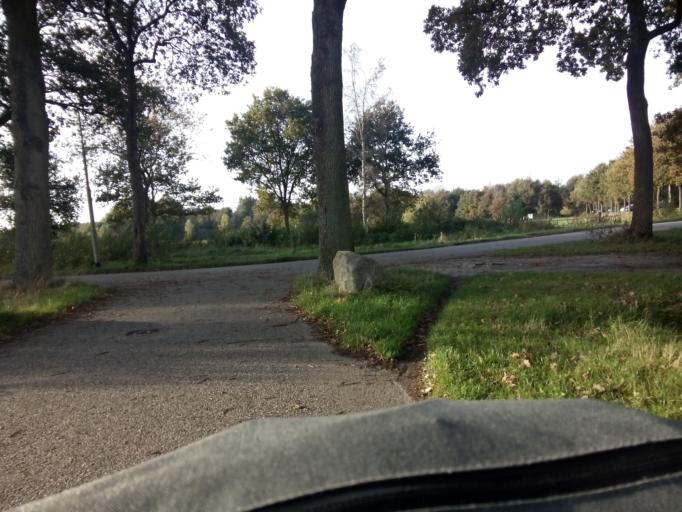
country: NL
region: Drenthe
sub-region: Gemeente Assen
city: Assen
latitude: 52.9842
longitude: 6.5244
